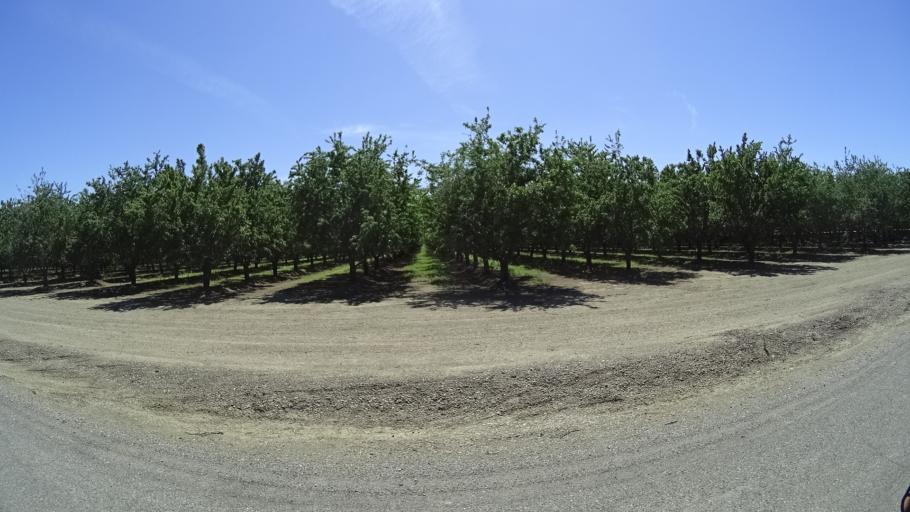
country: US
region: California
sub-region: Glenn County
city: Orland
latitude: 39.7322
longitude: -122.1187
